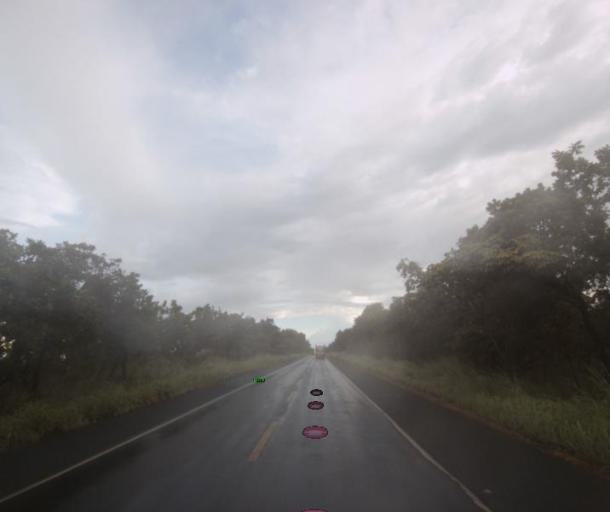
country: BR
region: Goias
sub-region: Porangatu
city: Porangatu
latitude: -13.8389
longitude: -49.0454
